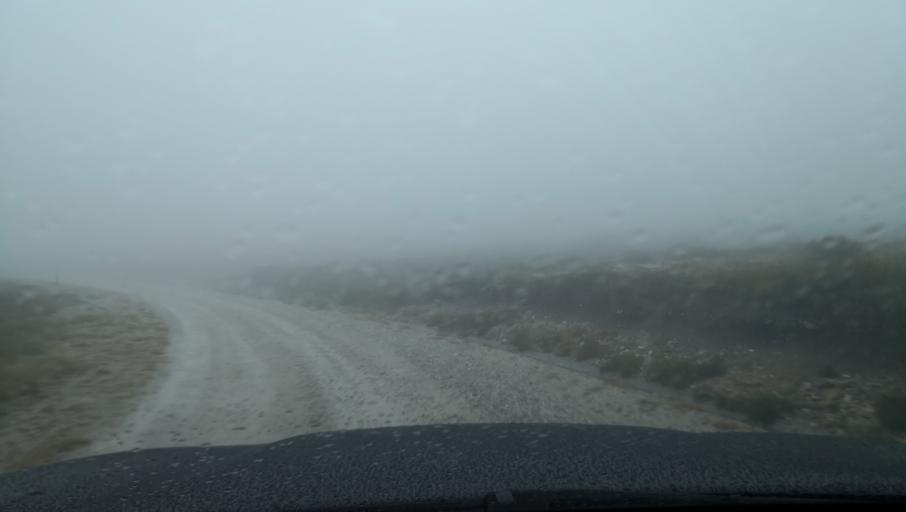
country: PT
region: Vila Real
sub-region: Vila Real
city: Vila Real
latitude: 41.3393
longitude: -7.8421
